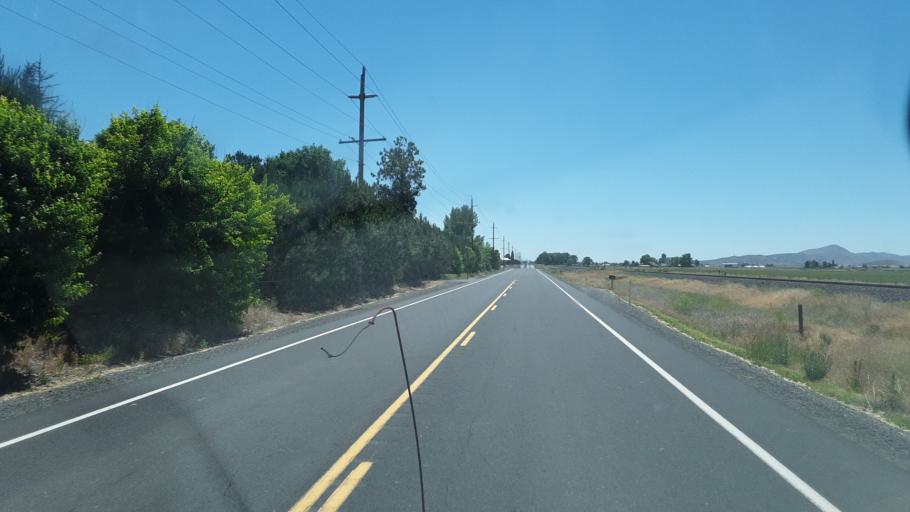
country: US
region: Oregon
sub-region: Klamath County
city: Altamont
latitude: 42.0513
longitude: -121.6389
